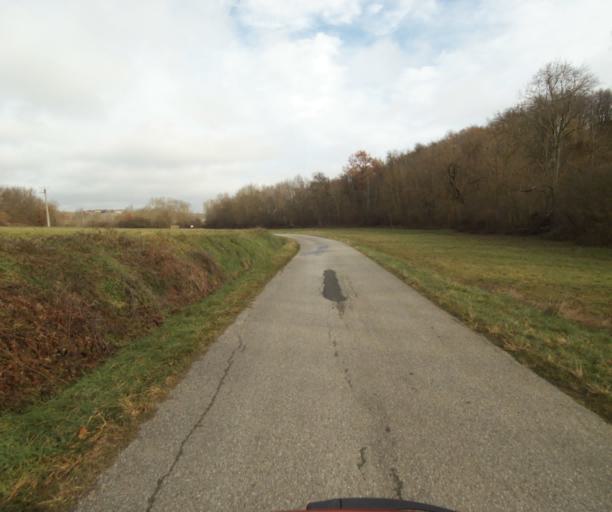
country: FR
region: Midi-Pyrenees
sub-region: Departement de l'Ariege
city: Saverdun
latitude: 43.1767
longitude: 1.5166
